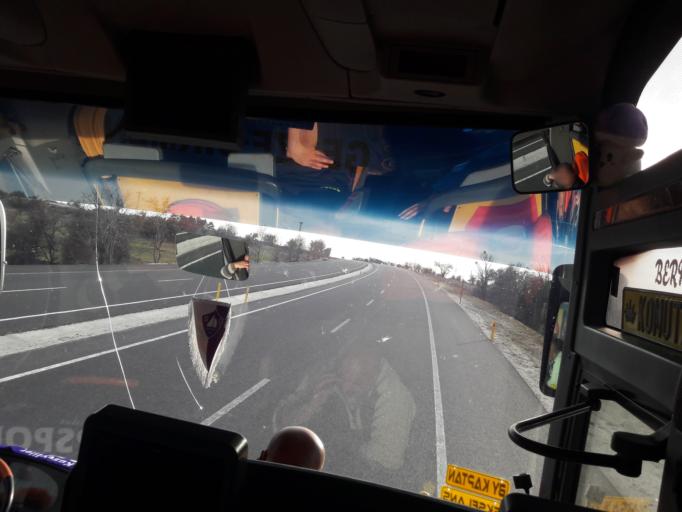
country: TR
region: Cankiri
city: Ilgaz
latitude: 40.8569
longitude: 33.6128
